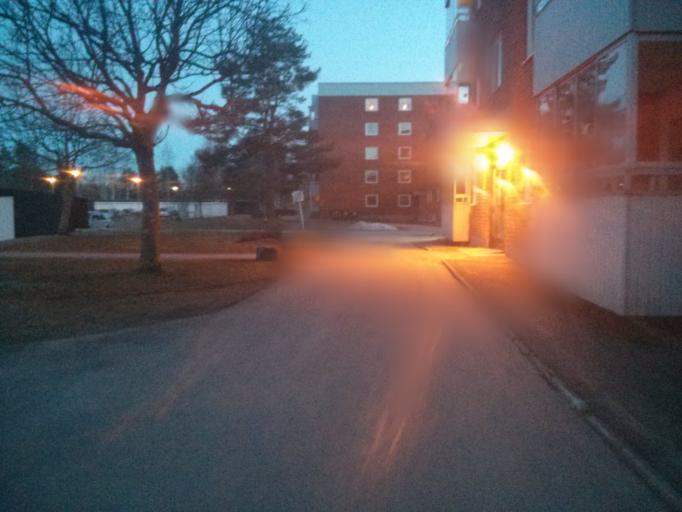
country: SE
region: Vaesternorrland
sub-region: Sundsvalls Kommun
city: Kvissleby
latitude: 62.2993
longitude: 17.3825
